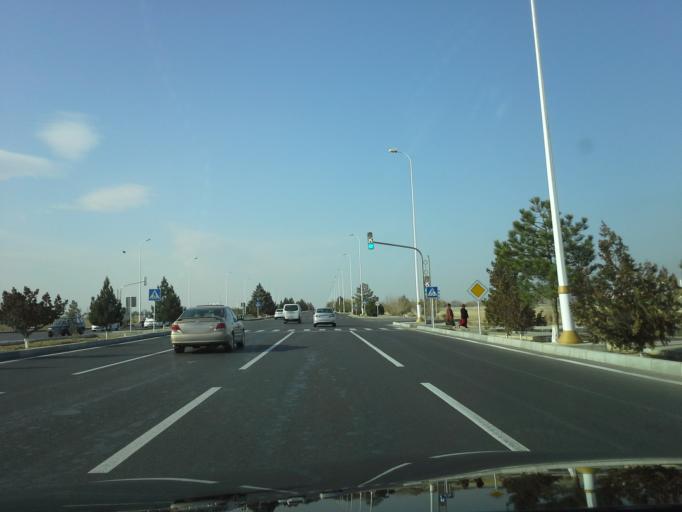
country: TM
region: Ahal
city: Ashgabat
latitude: 38.0003
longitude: 58.3000
